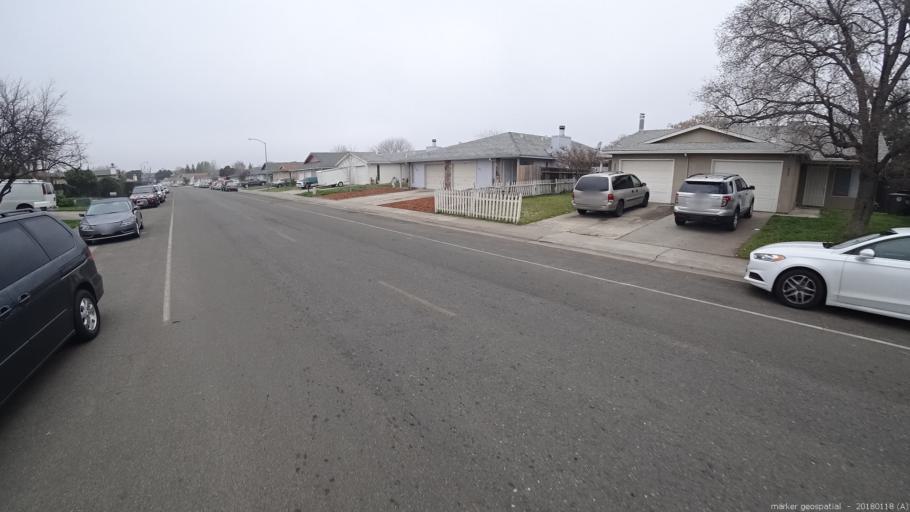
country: US
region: California
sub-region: Sacramento County
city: Rancho Cordova
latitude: 38.5813
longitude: -121.3015
